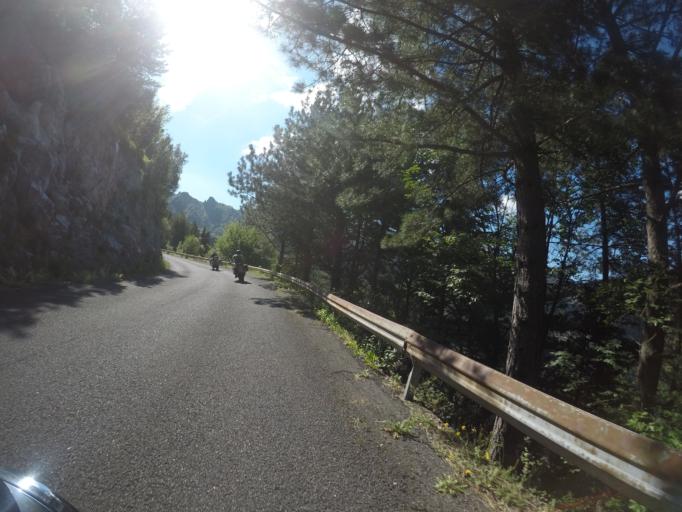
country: IT
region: Tuscany
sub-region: Provincia di Massa-Carrara
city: Montignoso
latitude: 44.0558
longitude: 10.1975
